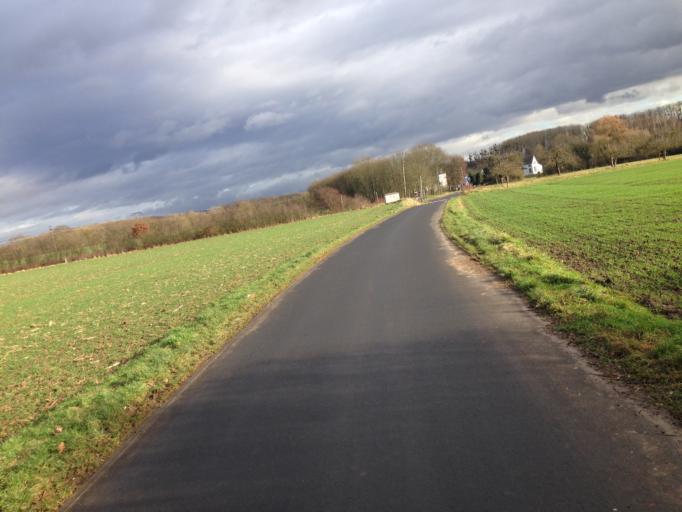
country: DE
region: Hesse
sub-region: Regierungsbezirk Giessen
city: Hungen
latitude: 50.4585
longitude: 8.9045
